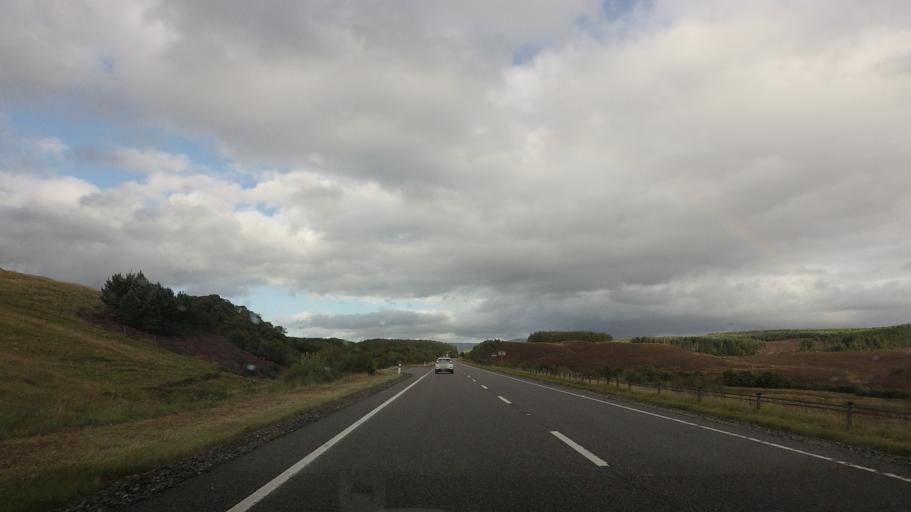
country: GB
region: Scotland
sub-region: Highland
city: Kingussie
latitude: 57.0627
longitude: -4.0775
